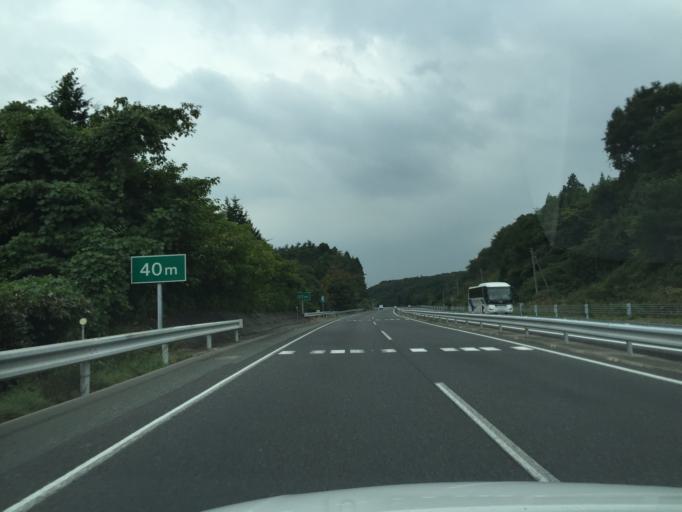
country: JP
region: Fukushima
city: Iwaki
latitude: 37.0625
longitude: 140.7966
